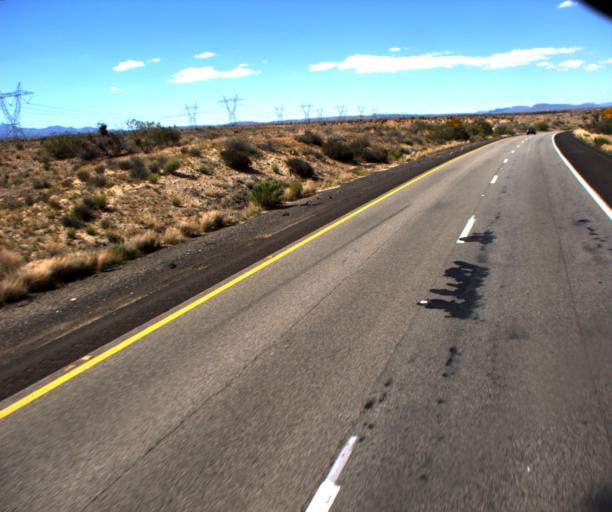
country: US
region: Arizona
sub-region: Mohave County
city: Kingman
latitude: 34.9651
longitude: -113.6702
